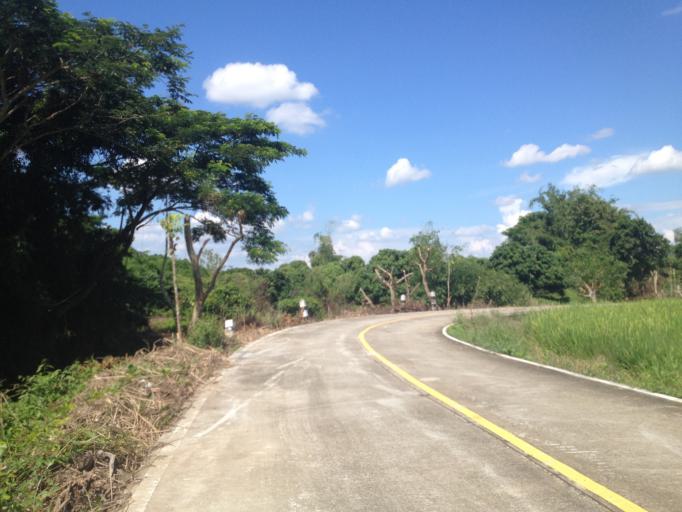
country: TH
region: Chiang Mai
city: Hang Dong
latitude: 18.6847
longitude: 98.9765
